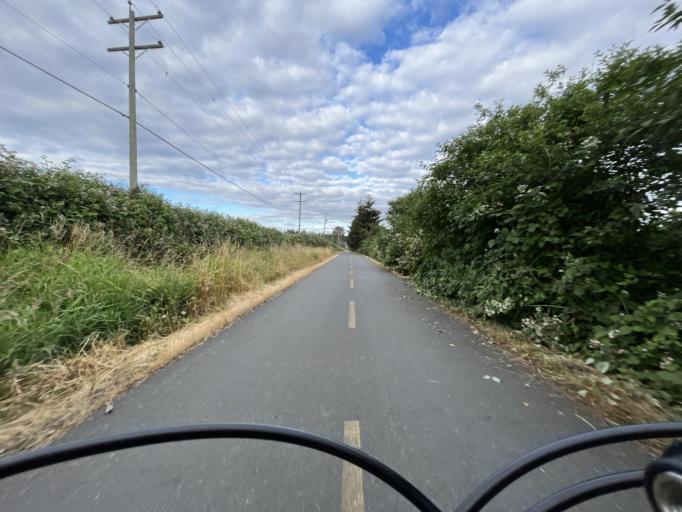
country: CA
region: British Columbia
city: Victoria
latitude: 48.4762
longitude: -123.3573
